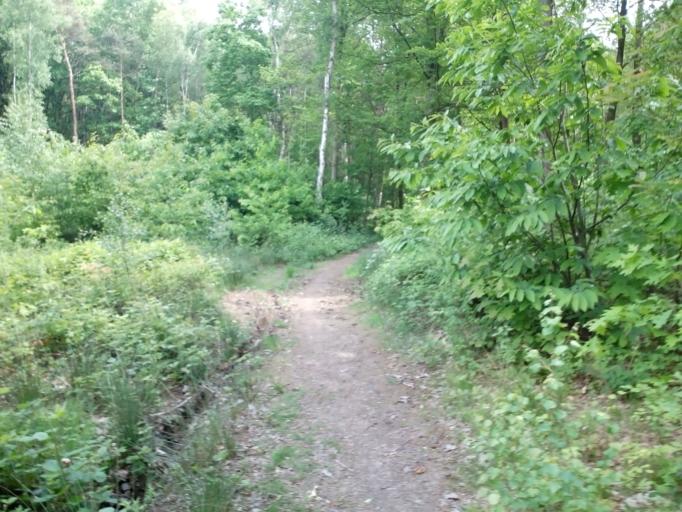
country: BE
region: Flanders
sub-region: Provincie Vlaams-Brabant
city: Bertem
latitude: 50.8814
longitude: 4.6134
